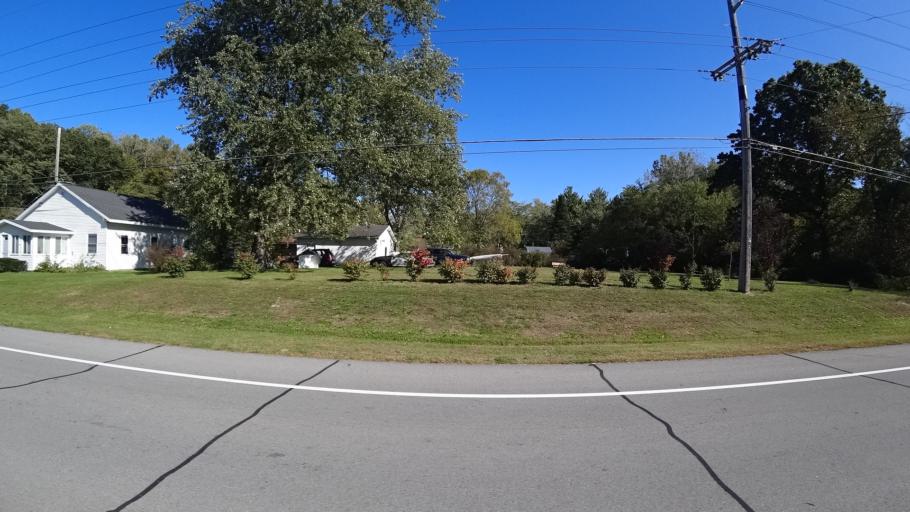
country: US
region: Indiana
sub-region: LaPorte County
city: Long Beach
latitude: 41.7236
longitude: -86.8554
